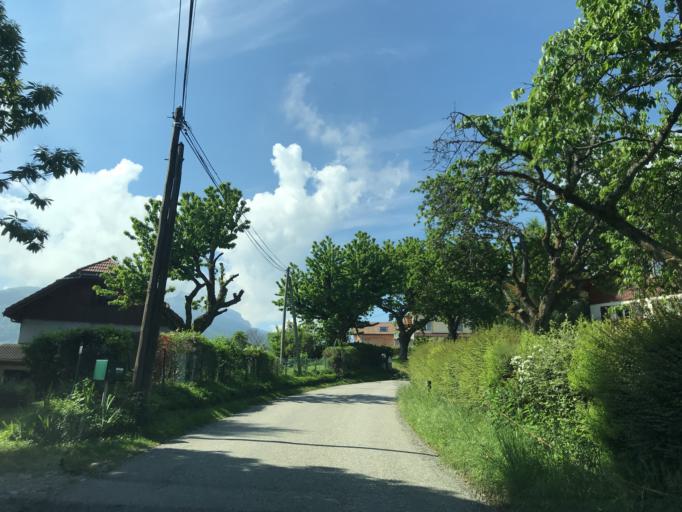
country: FR
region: Rhone-Alpes
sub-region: Departement de la Savoie
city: Vimines
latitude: 45.5496
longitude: 5.8703
